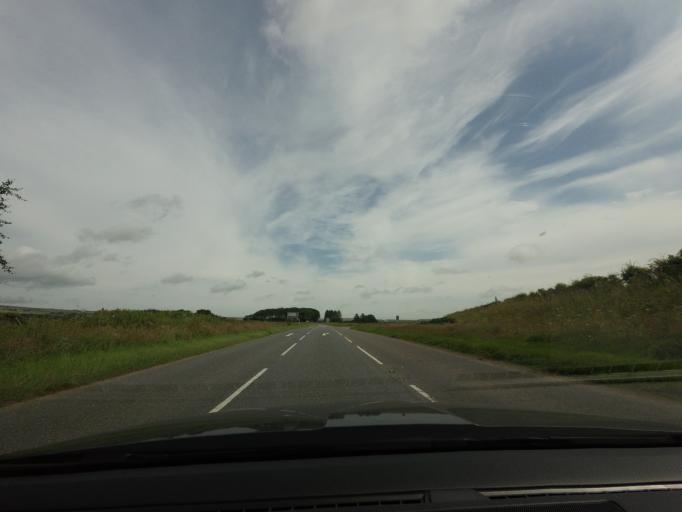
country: GB
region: Scotland
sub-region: Aberdeenshire
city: Rosehearty
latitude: 57.6028
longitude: -2.2204
